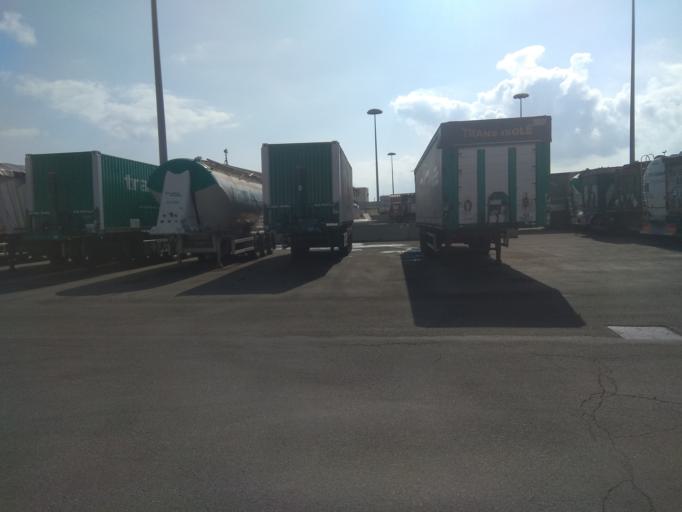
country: IT
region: Sardinia
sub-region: Provincia di Cagliari
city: Cagliari
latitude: 39.2128
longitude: 9.1061
